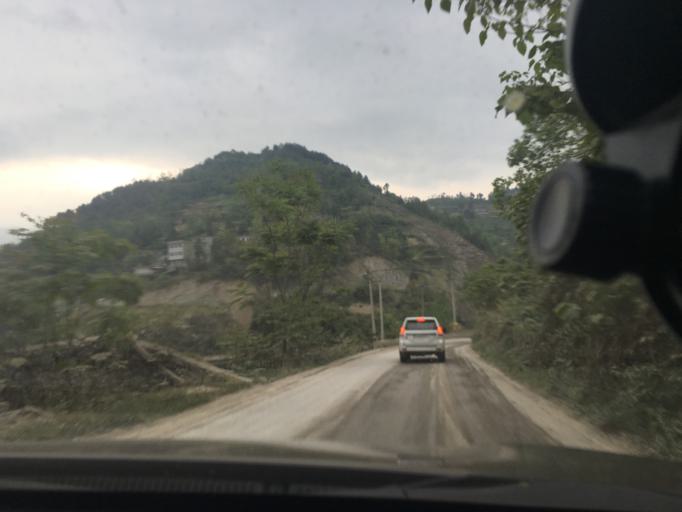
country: CN
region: Guizhou Sheng
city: Changbao
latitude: 28.1940
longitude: 108.2500
